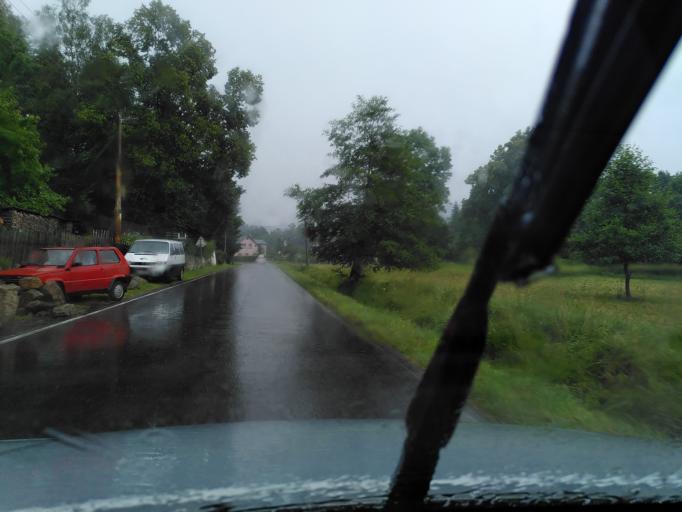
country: CZ
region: Ustecky
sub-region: Okres Decin
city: Chribska
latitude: 50.8161
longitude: 14.5260
